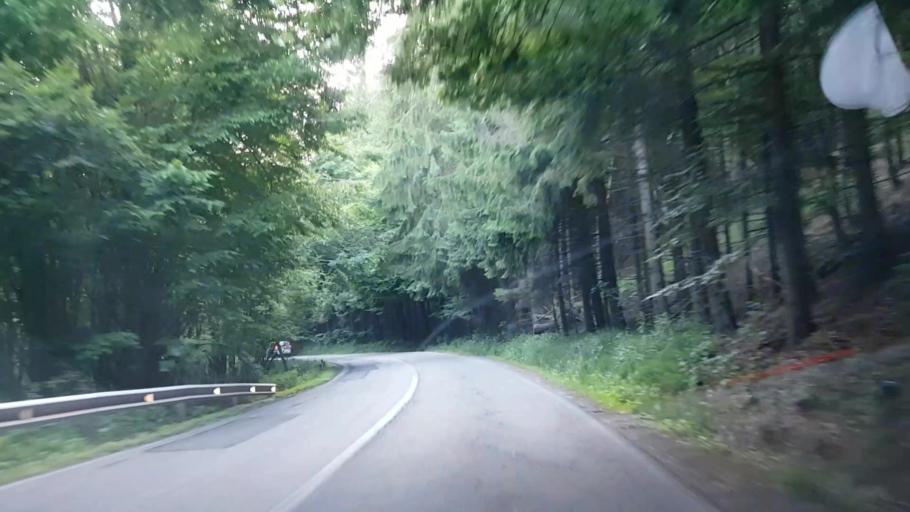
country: RO
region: Harghita
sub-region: Comuna Praid
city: Ocna de Sus
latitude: 46.5814
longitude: 25.2389
